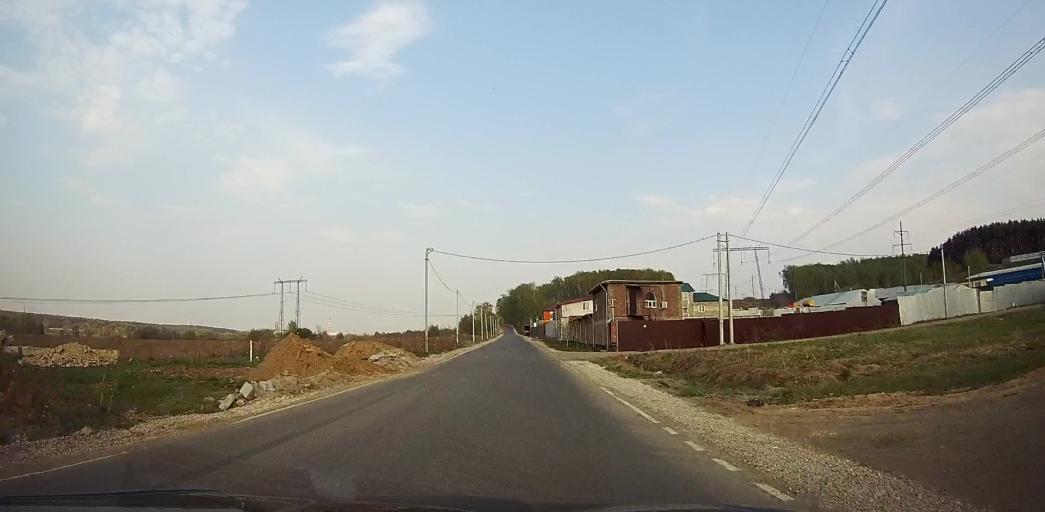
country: RU
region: Moskovskaya
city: Lytkarino
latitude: 55.5595
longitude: 37.8923
